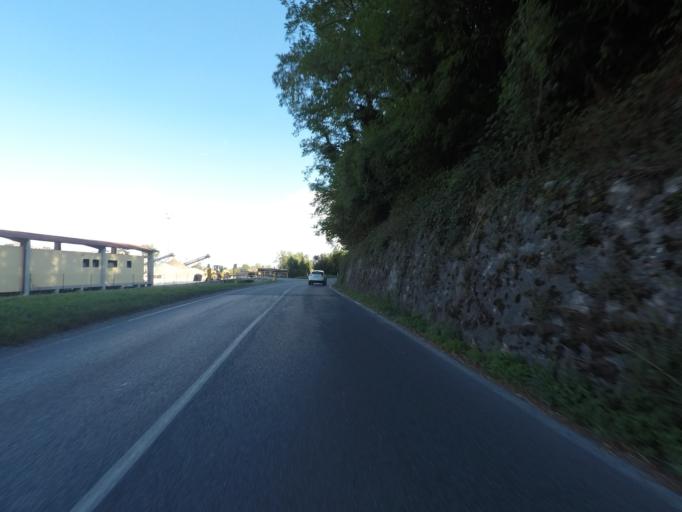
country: IT
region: Tuscany
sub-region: Provincia di Lucca
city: Lucca
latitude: 43.8779
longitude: 10.5216
